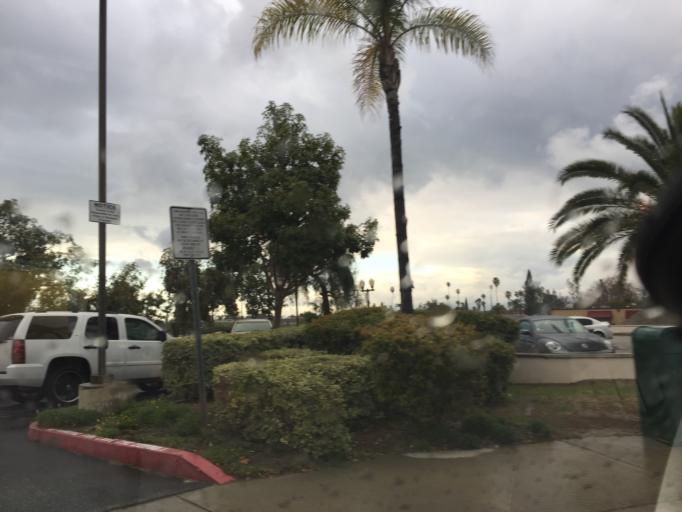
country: US
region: California
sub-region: San Bernardino County
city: Redlands
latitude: 34.0586
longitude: -117.1843
